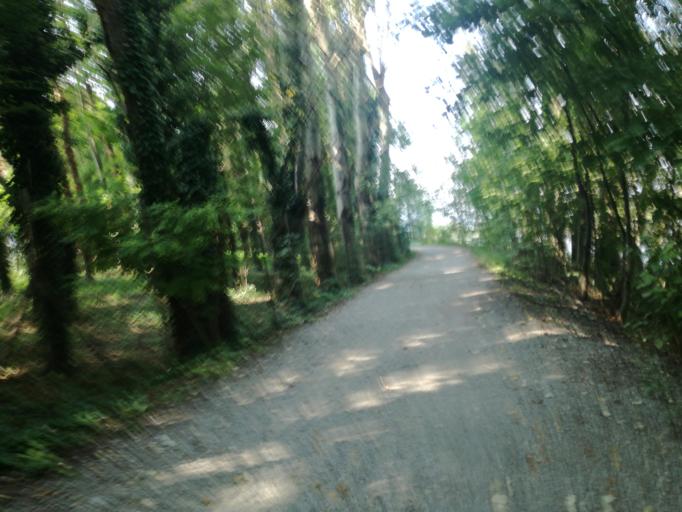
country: IT
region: Lombardy
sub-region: Provincia di Lecco
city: Airuno
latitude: 45.7549
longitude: 9.4450
